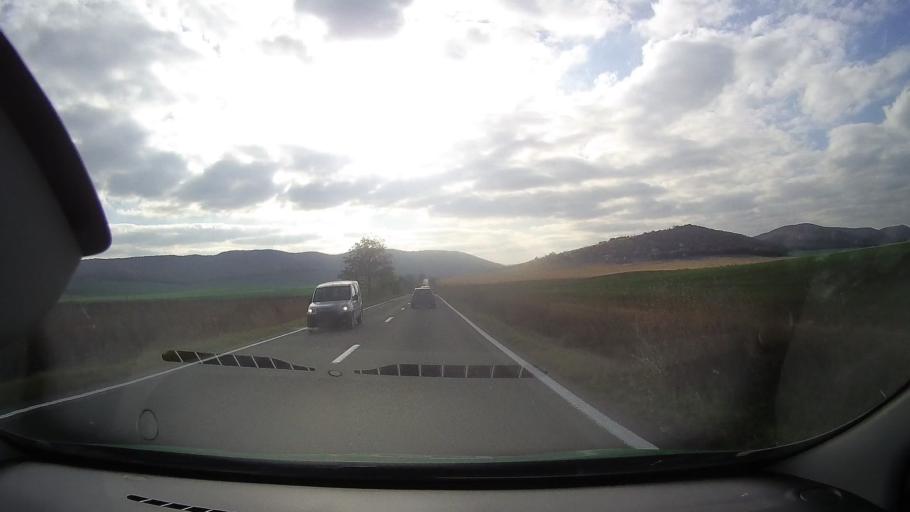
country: RO
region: Tulcea
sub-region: Comuna Nalbant
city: Nicolae Balcescu
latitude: 44.9765
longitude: 28.5452
